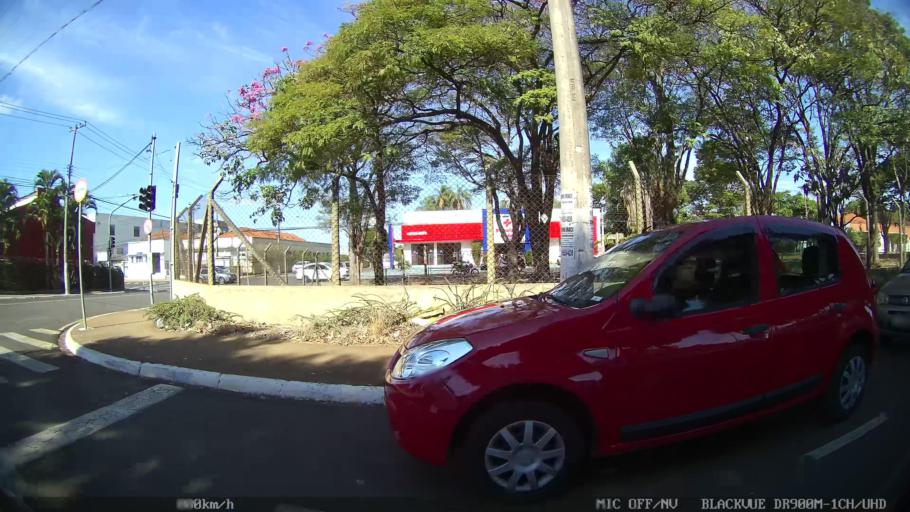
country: BR
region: Sao Paulo
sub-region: Franca
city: Franca
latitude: -20.5389
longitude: -47.4158
